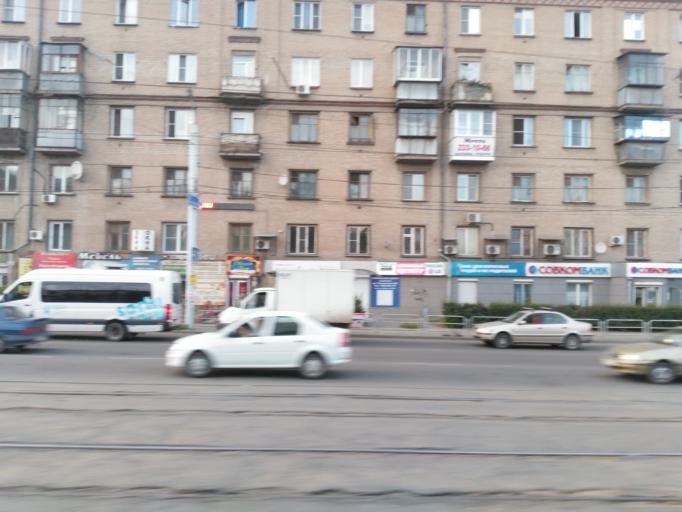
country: RU
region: Chelyabinsk
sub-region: Gorod Chelyabinsk
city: Chelyabinsk
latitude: 55.1842
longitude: 61.3956
